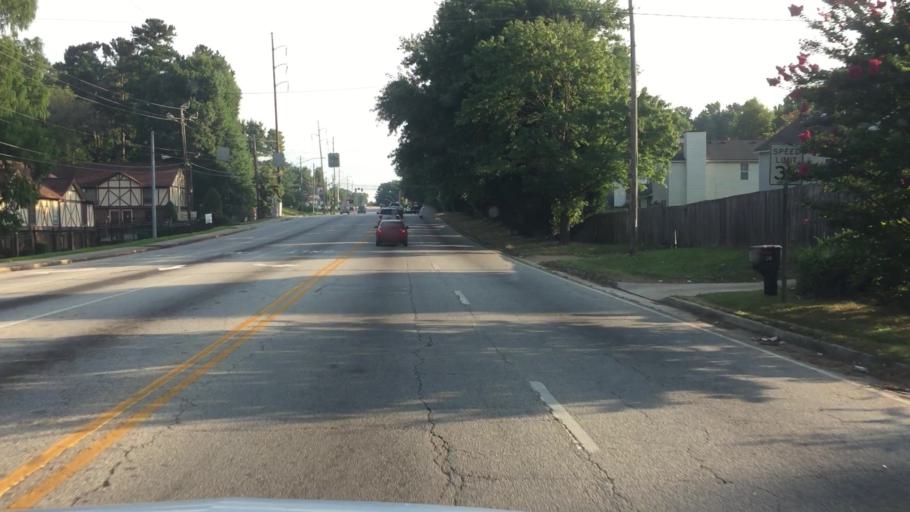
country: US
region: Georgia
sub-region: DeKalb County
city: Panthersville
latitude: 33.7122
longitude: -84.2524
